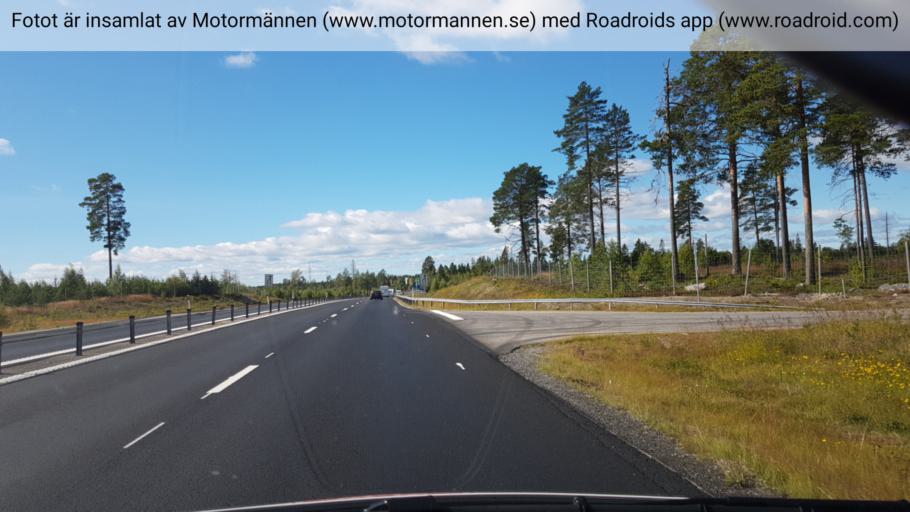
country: SE
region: Vaesterbotten
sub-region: Umea Kommun
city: Hoernefors
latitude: 63.6333
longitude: 19.8899
